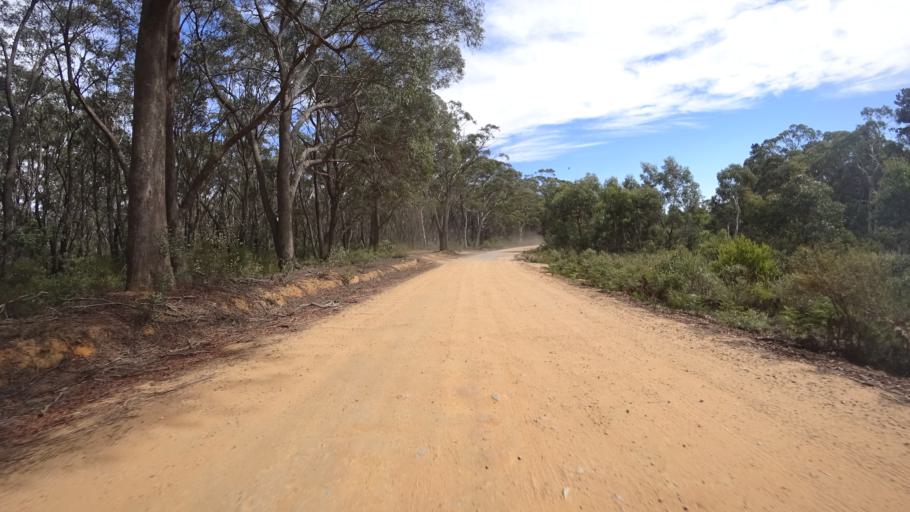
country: AU
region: New South Wales
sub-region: Lithgow
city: Lithgow
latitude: -33.3358
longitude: 150.2497
